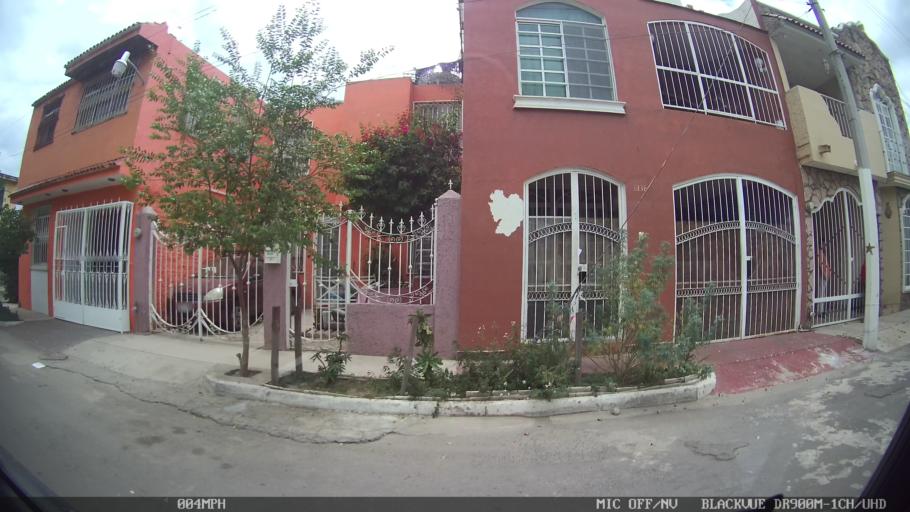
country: MX
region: Jalisco
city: Tonala
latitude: 20.6397
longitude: -103.2542
